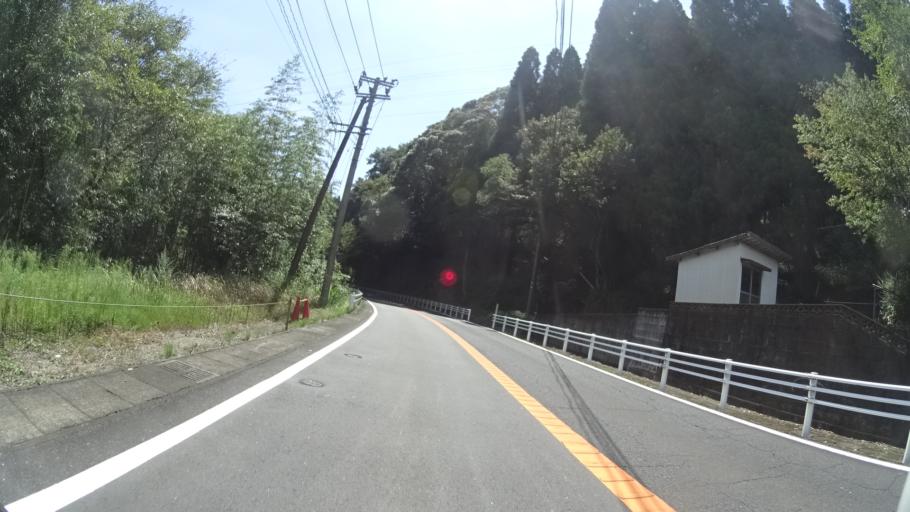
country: JP
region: Kagoshima
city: Kokubu-matsuki
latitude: 31.8452
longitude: 130.7527
